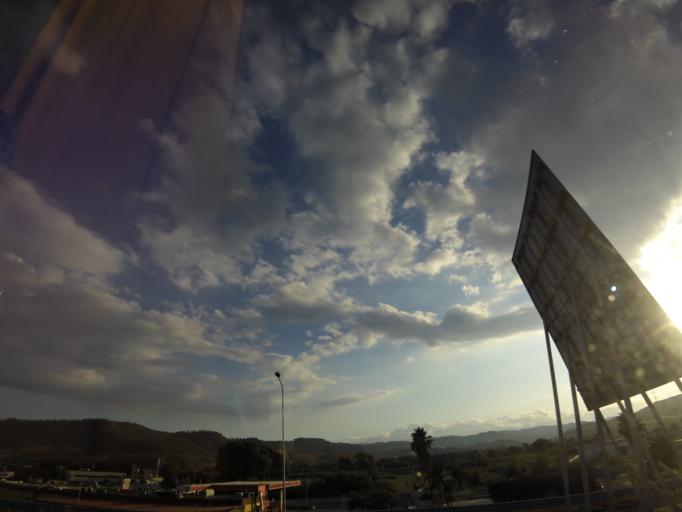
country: IT
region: Calabria
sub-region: Provincia di Catanzaro
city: Catanzaro
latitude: 38.8621
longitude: 16.5685
